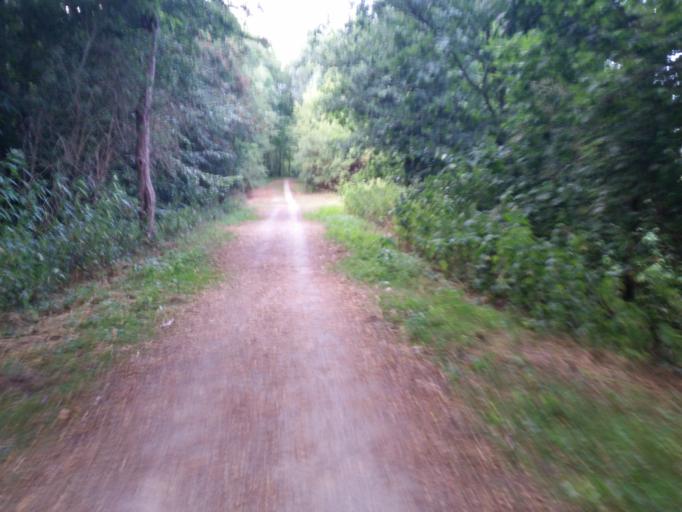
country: BE
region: Flanders
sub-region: Provincie Vlaams-Brabant
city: Zemst
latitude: 50.9772
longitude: 4.4860
